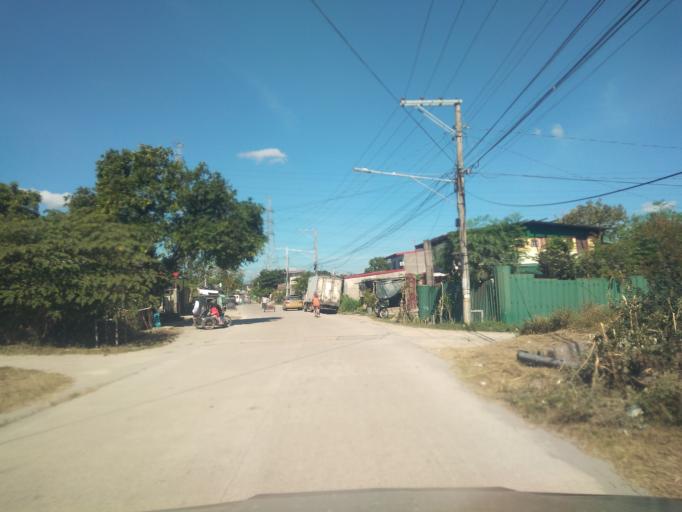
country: PH
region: Central Luzon
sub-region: Province of Pampanga
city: Bacolor
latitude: 15.0013
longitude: 120.6483
